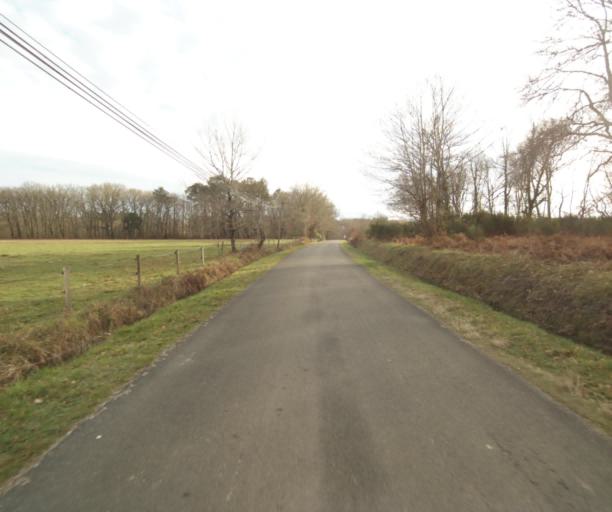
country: FR
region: Aquitaine
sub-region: Departement des Landes
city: Gabarret
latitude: 44.0216
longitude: 0.0476
